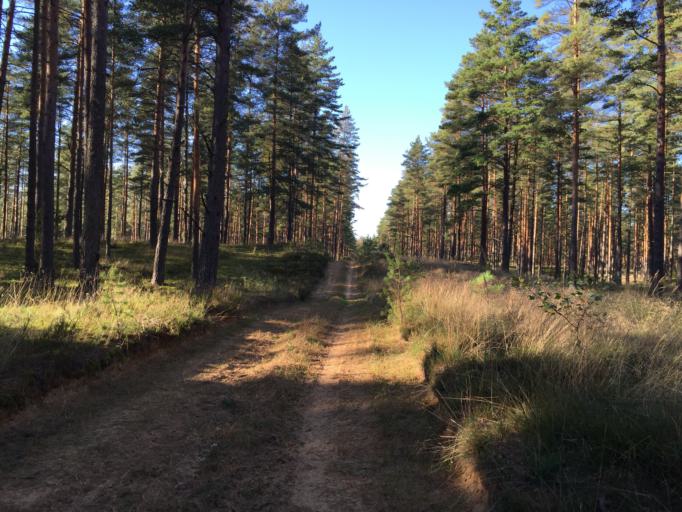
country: LV
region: Garkalne
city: Garkalne
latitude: 57.0203
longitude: 24.3662
